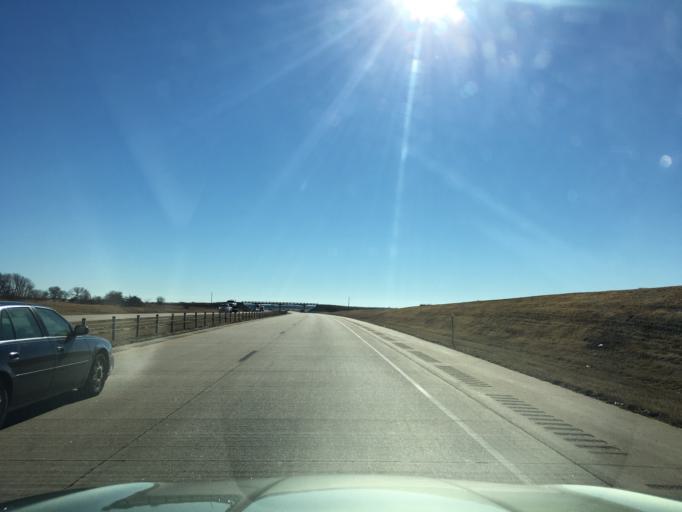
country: US
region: Oklahoma
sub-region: Kay County
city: Tonkawa
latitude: 36.5107
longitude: -97.3372
